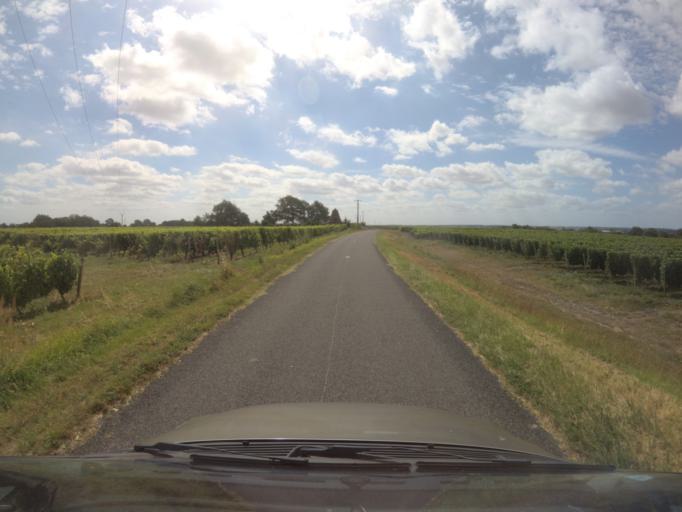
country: FR
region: Pays de la Loire
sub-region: Departement de Maine-et-Loire
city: Saint-Jean
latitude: 47.1882
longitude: -0.3569
